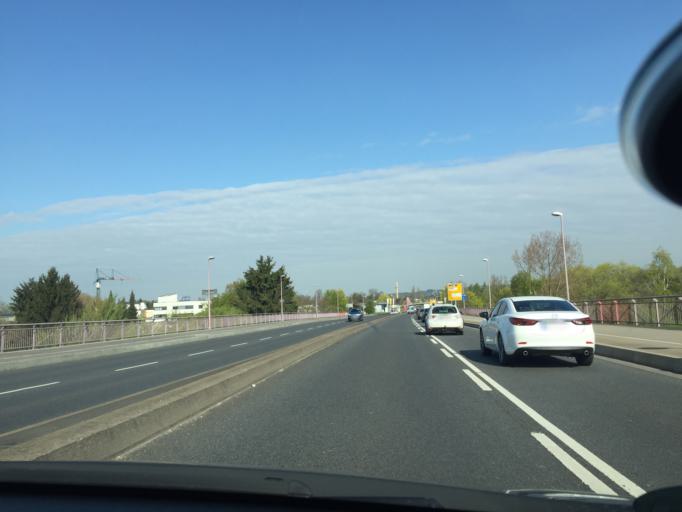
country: DE
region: Bavaria
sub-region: Regierungsbezirk Unterfranken
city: Aschaffenburg
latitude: 49.9669
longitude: 9.1374
